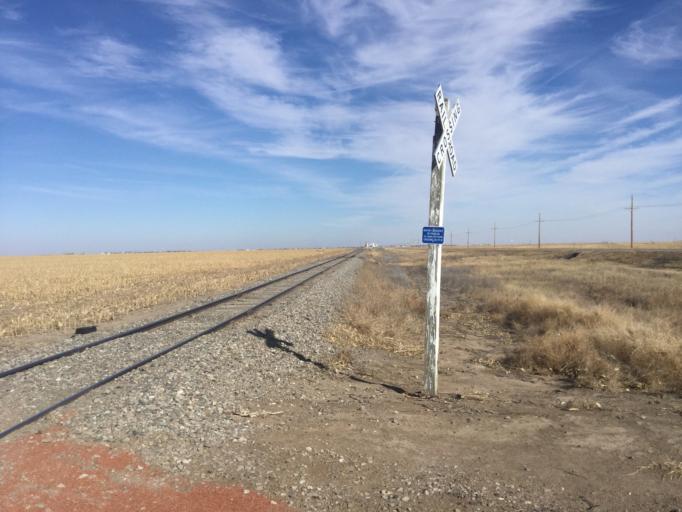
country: US
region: Kansas
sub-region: Haskell County
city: Satanta
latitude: 37.4610
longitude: -100.9256
